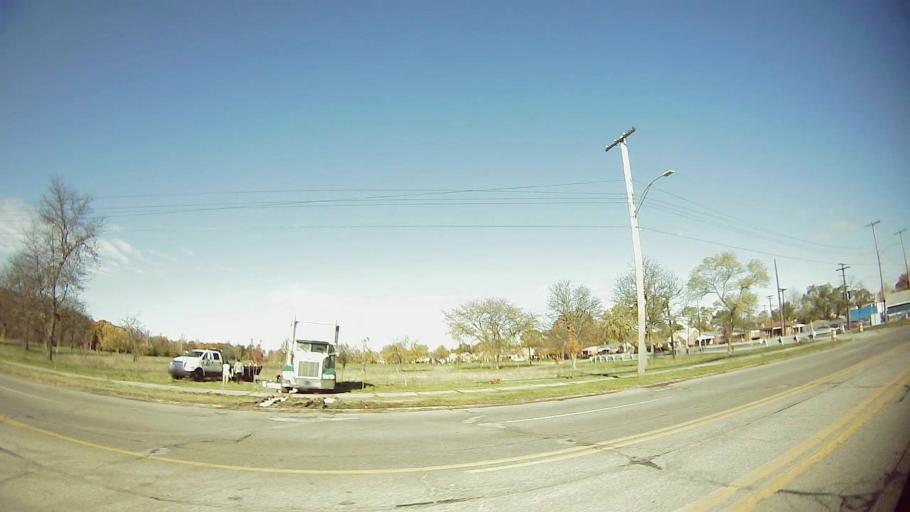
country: US
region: Michigan
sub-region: Wayne County
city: Dearborn Heights
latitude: 42.3429
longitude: -83.2443
